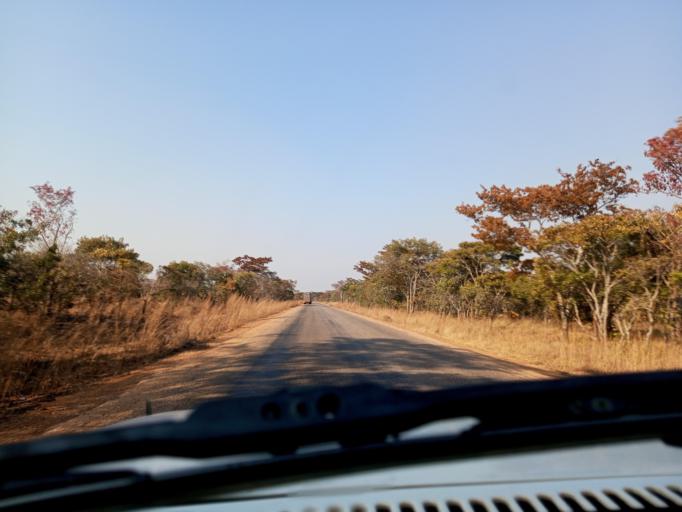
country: ZM
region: Northern
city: Mpika
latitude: -12.4218
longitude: 31.0790
